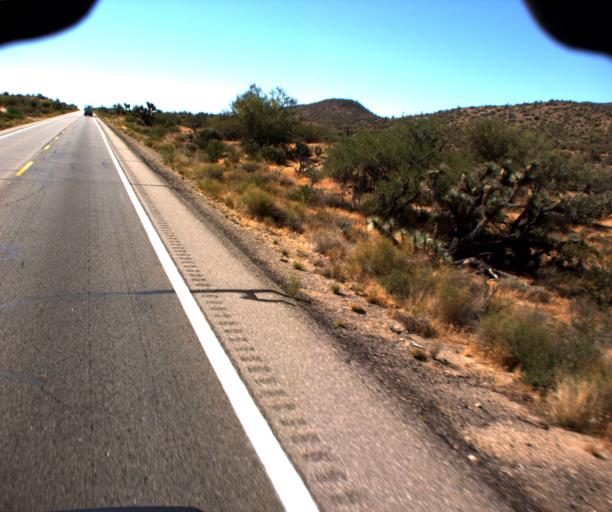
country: US
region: Arizona
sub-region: Yavapai County
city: Bagdad
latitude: 34.3543
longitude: -113.1672
